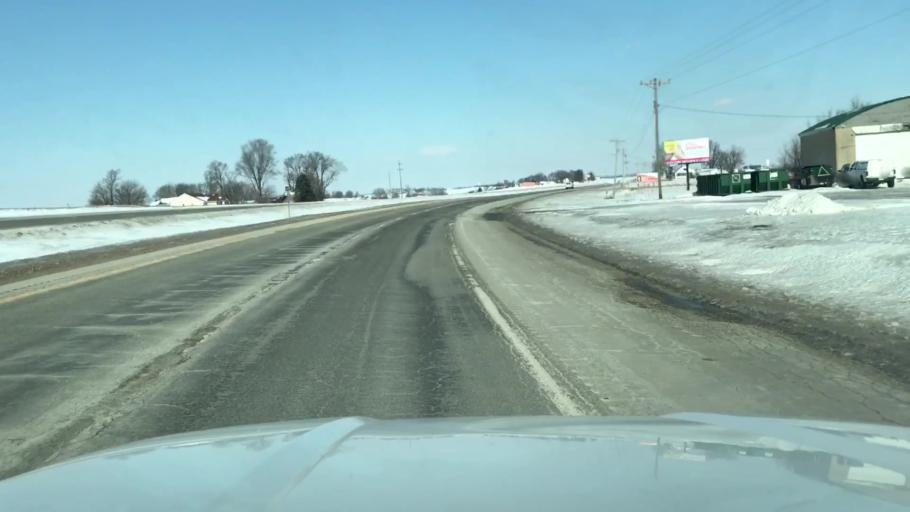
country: US
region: Missouri
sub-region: Nodaway County
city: Maryville
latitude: 40.2793
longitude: -94.8753
